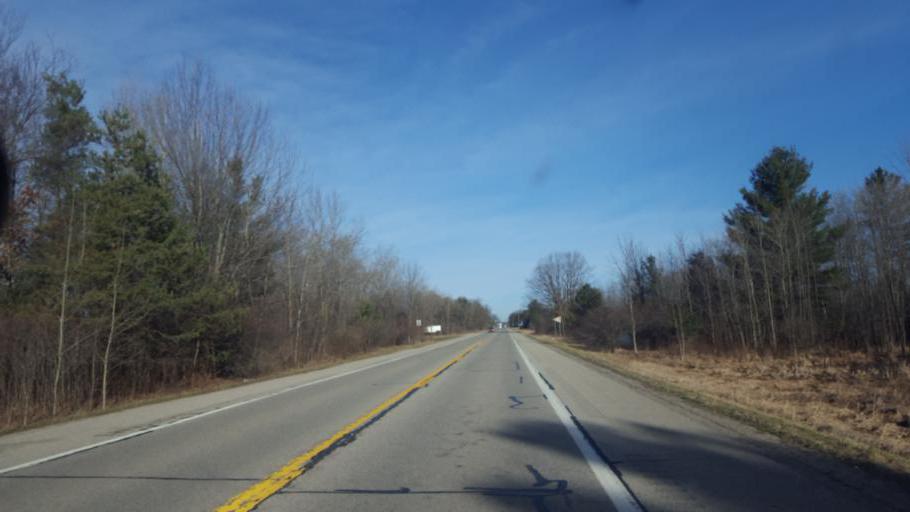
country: US
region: Michigan
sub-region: Montcalm County
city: Edmore
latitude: 43.4101
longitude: -85.1189
